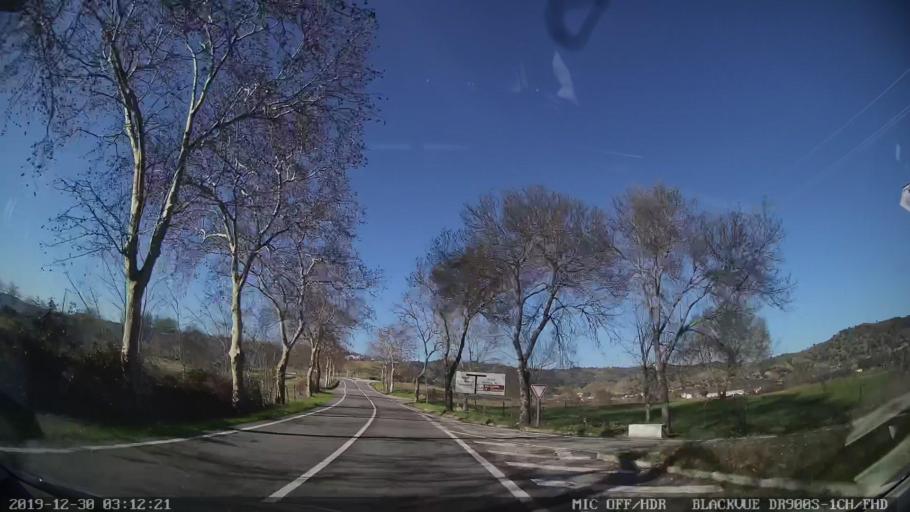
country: PT
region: Castelo Branco
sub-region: Idanha-A-Nova
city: Idanha-a-Nova
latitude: 39.9096
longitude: -7.2199
